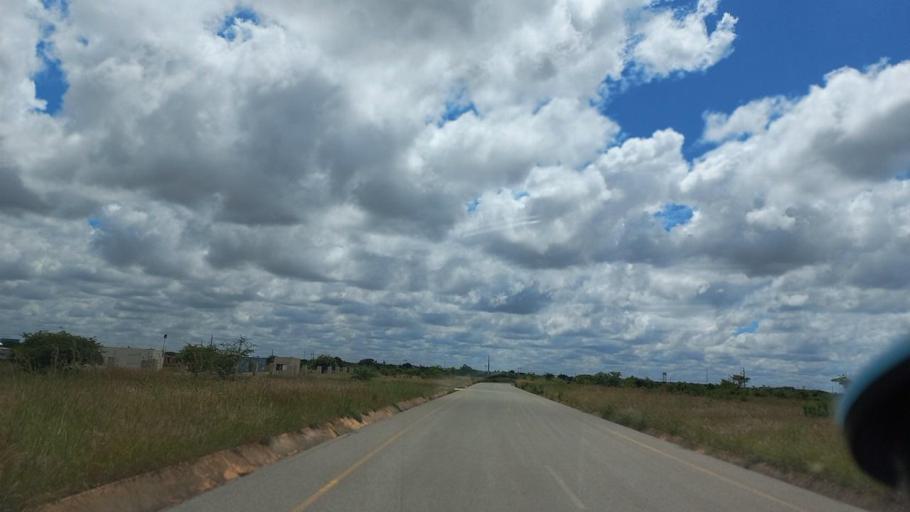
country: ZM
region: Lusaka
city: Lusaka
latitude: -15.4943
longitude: 28.3749
